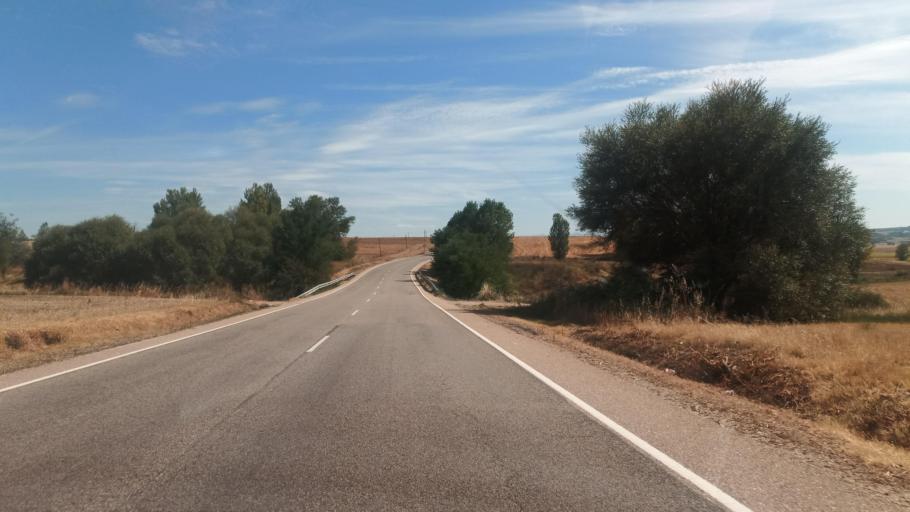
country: ES
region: Castille and Leon
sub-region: Provincia de Burgos
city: Quintanabureba
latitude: 42.6269
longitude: -3.3735
